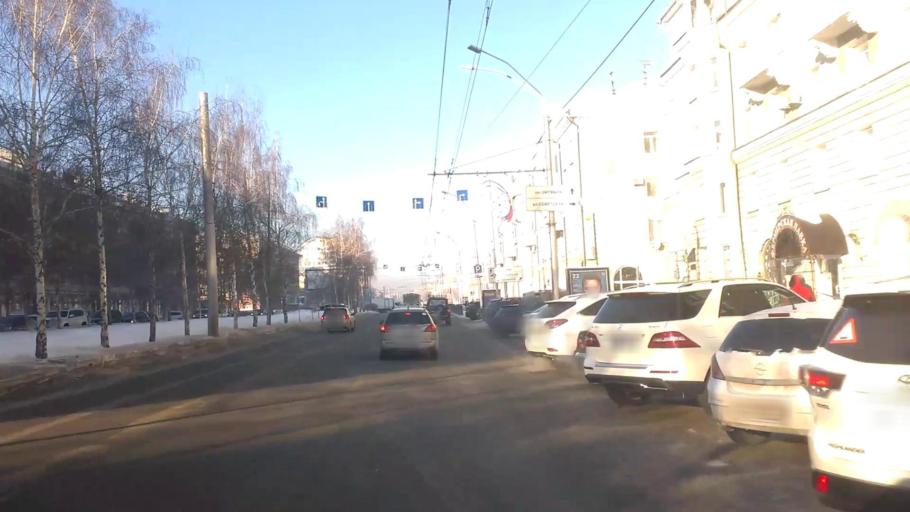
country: RU
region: Altai Krai
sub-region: Gorod Barnaulskiy
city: Barnaul
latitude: 53.3533
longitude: 83.7716
